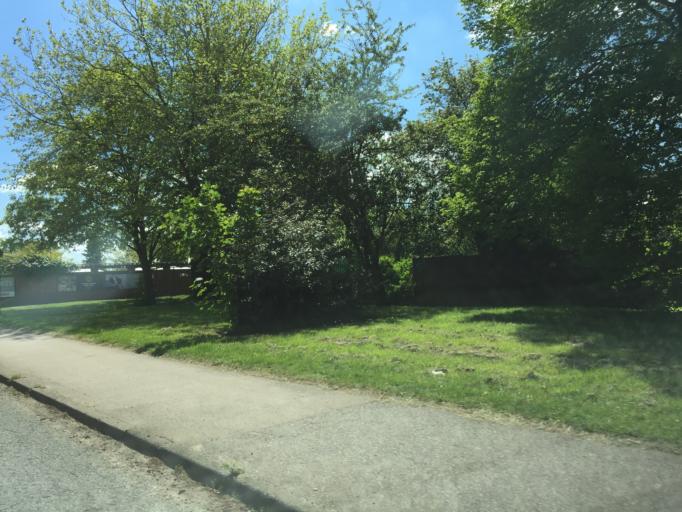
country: GB
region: England
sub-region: Milton Keynes
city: Woburn Sands
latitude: 52.0216
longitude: -0.6587
